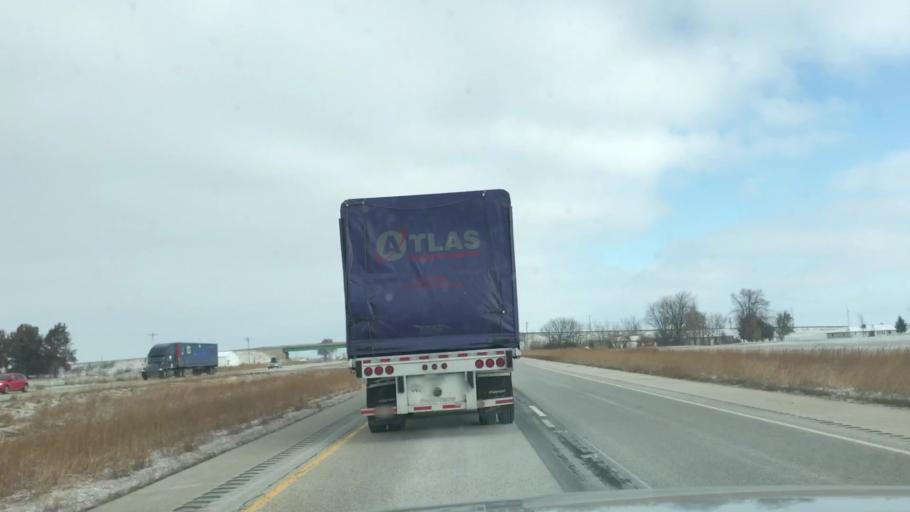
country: US
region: Illinois
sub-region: Sangamon County
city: Divernon
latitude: 39.5210
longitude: -89.6454
